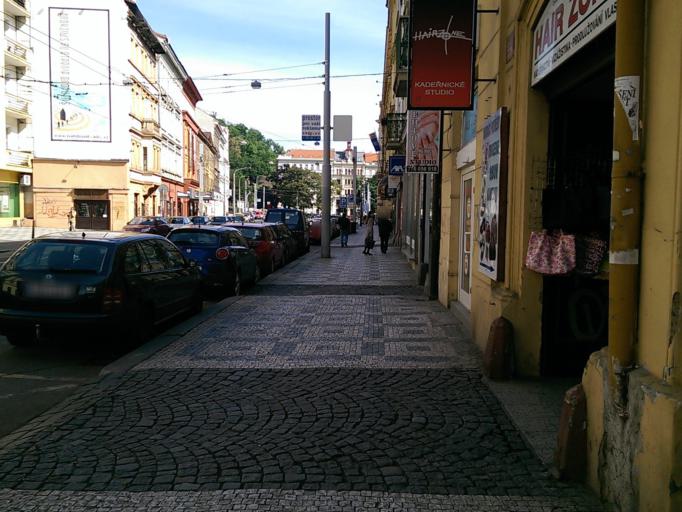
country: CZ
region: Praha
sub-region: Praha 1
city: Mala Strana
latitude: 50.0770
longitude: 14.4044
